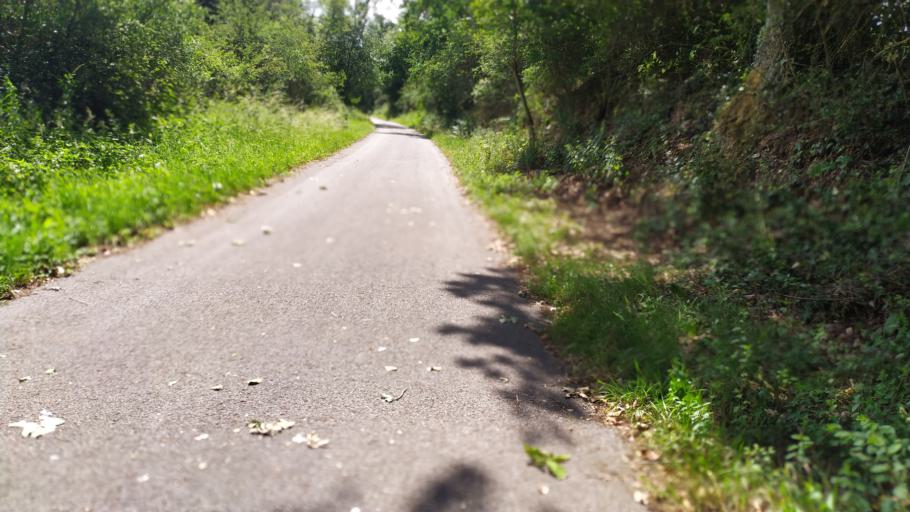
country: BE
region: Wallonia
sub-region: Province de Namur
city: Houyet
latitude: 50.1646
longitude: 5.0557
